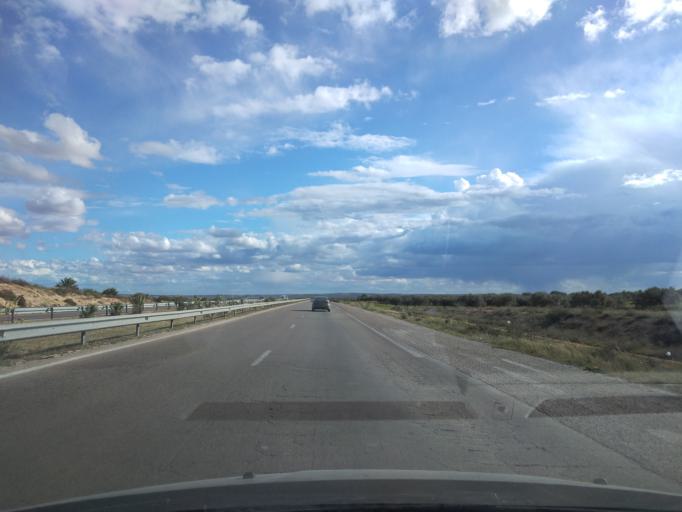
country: TN
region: Al Munastir
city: Manzil Kamil
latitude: 35.6107
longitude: 10.5972
